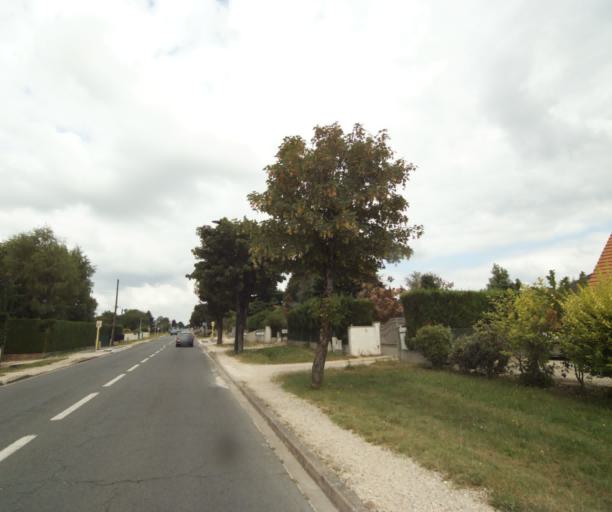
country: FR
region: Centre
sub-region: Departement du Loiret
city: Checy
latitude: 47.8996
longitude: 2.0140
